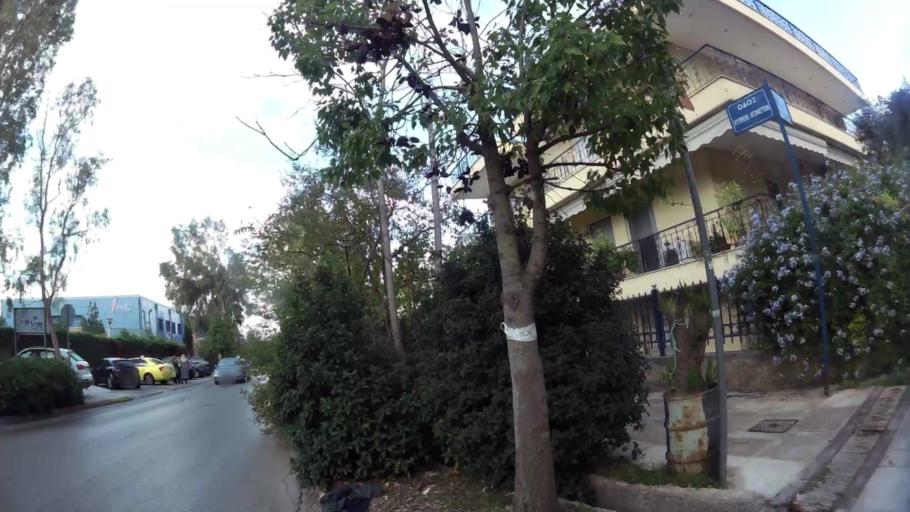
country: GR
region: Attica
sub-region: Nomarchia Athinas
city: Vrilissia
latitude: 38.0404
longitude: 23.8216
